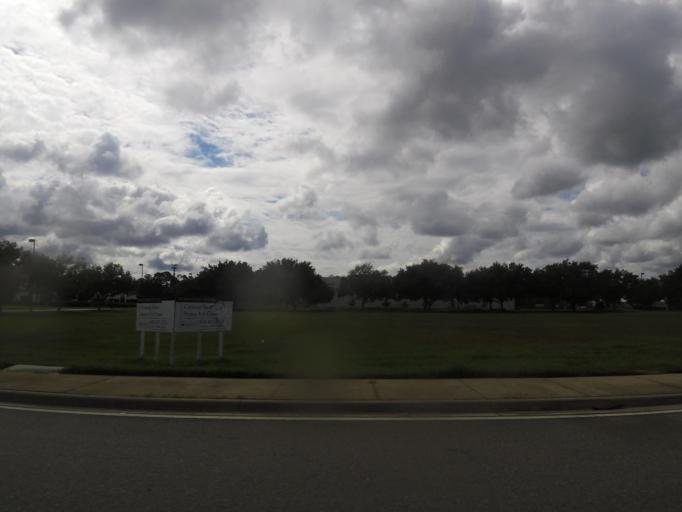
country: US
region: Florida
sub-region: Saint Johns County
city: Villano Beach
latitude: 29.9880
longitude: -81.4535
